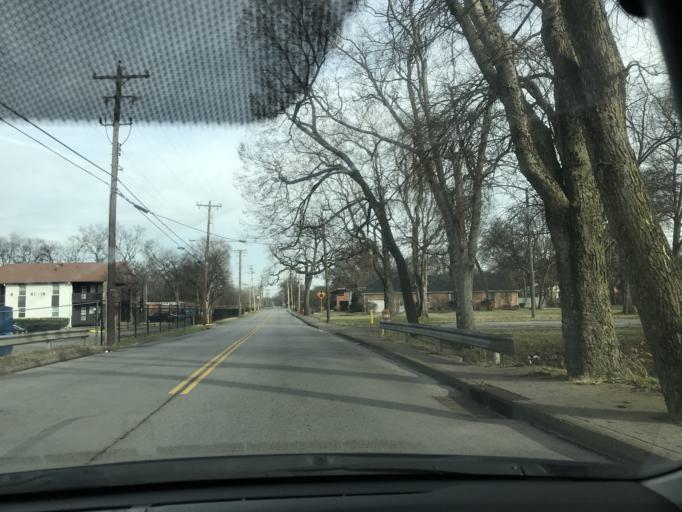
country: US
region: Tennessee
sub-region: Davidson County
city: Nashville
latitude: 36.1698
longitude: -86.8194
